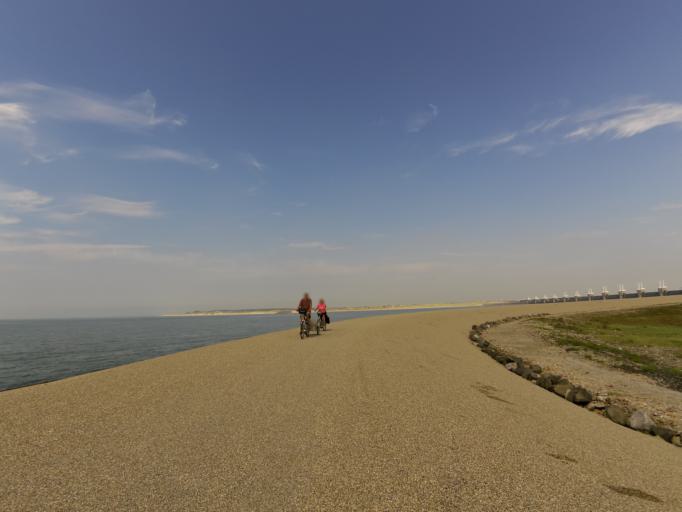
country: NL
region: Zeeland
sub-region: Schouwen-Duiveland
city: Burgh
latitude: 51.6537
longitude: 3.7158
